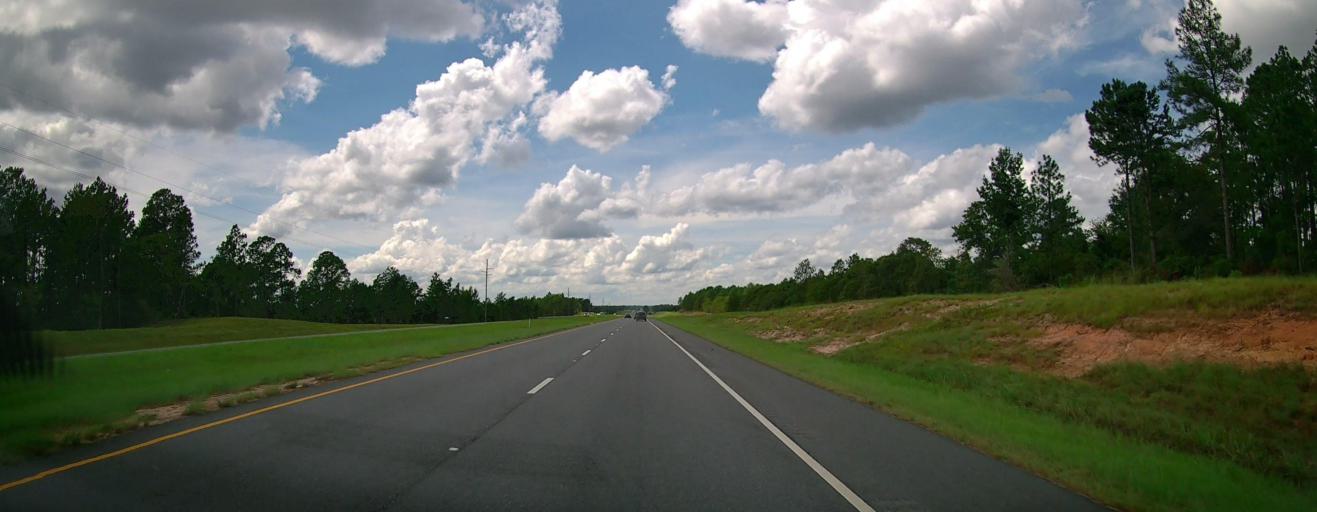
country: US
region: Georgia
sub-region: Taylor County
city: Butler
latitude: 32.5801
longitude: -84.3208
